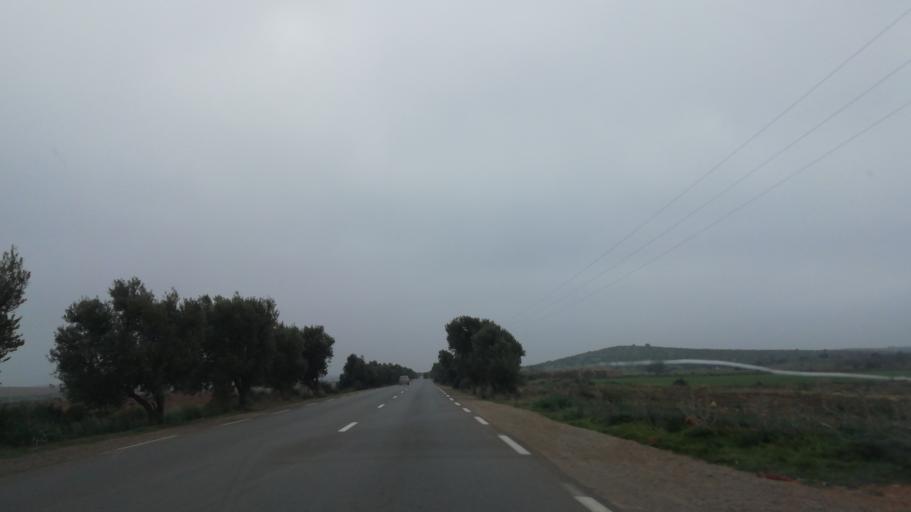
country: DZ
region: Mascara
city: Mascara
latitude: 35.3118
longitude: 0.3930
